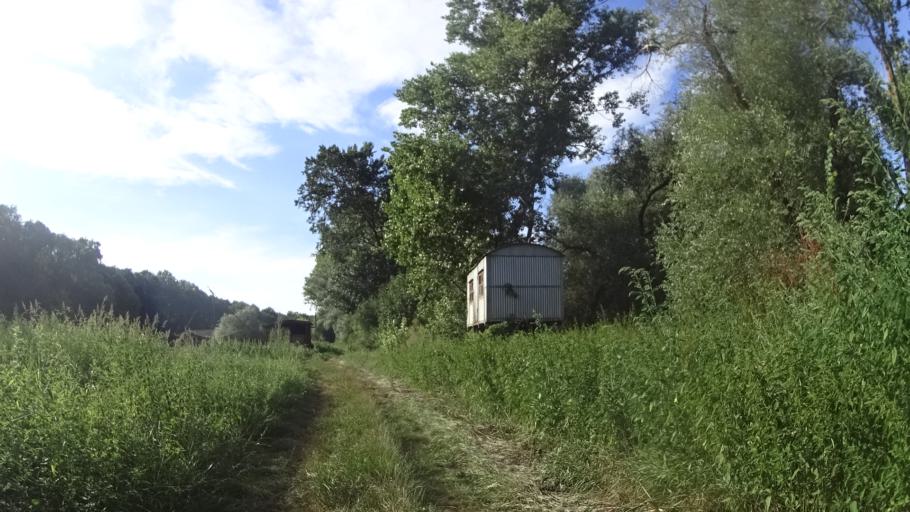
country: AT
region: Lower Austria
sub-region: Politischer Bezirk Mistelbach
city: Rabensburg
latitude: 48.6112
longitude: 16.9422
